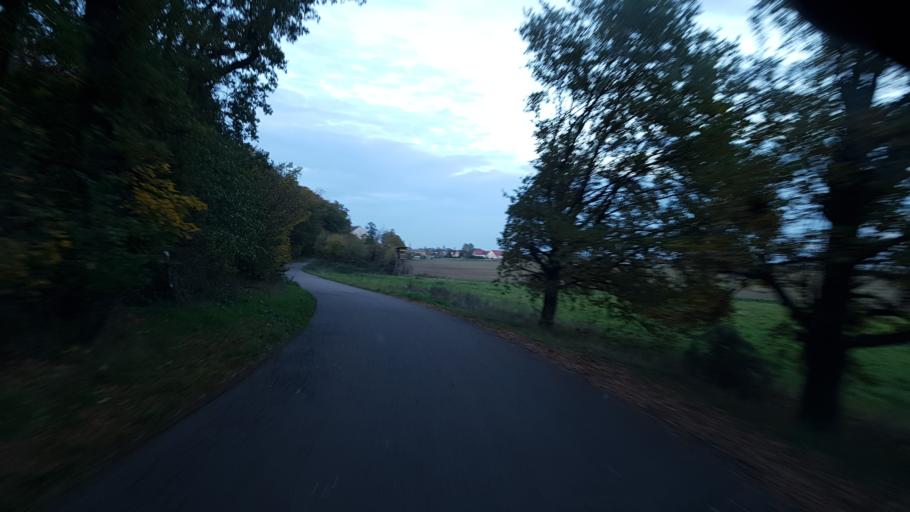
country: DE
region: Brandenburg
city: Muhlberg
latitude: 51.4383
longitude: 13.1723
